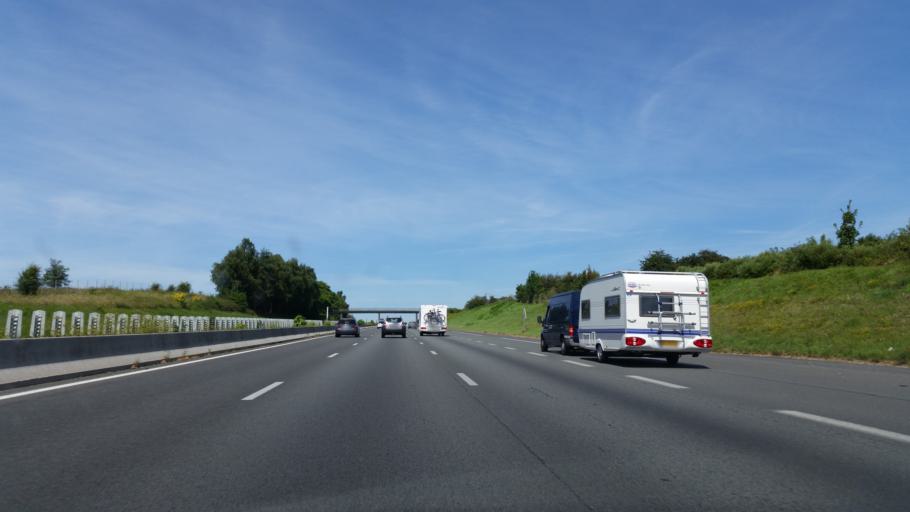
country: FR
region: Nord-Pas-de-Calais
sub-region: Departement du Pas-de-Calais
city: Croisilles
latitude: 50.1956
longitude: 2.8701
